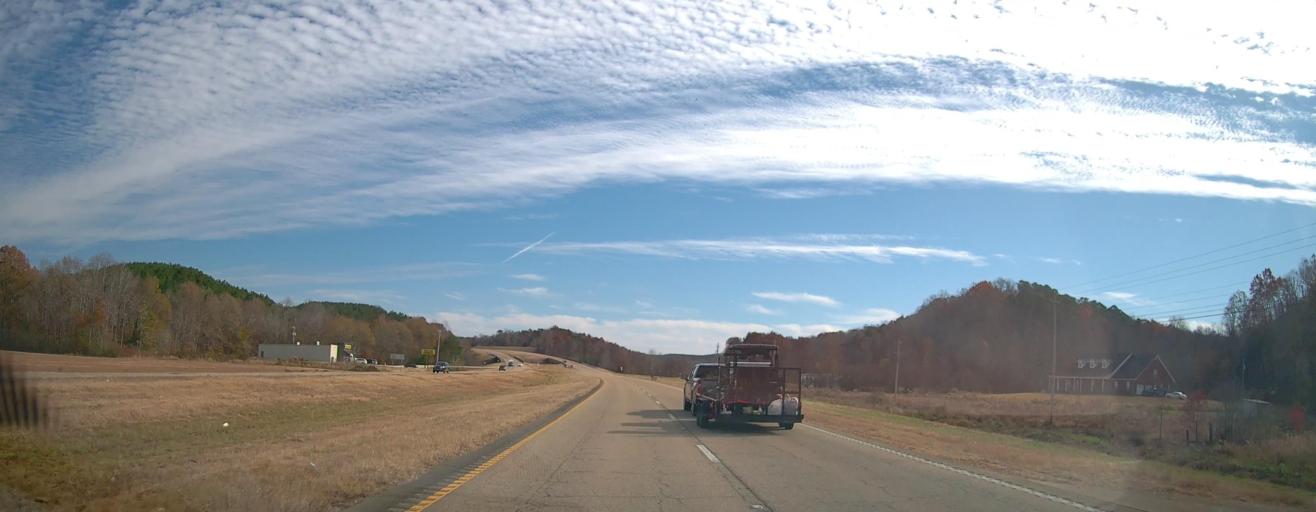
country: US
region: Mississippi
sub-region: Alcorn County
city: Corinth
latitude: 34.9351
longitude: -88.7728
